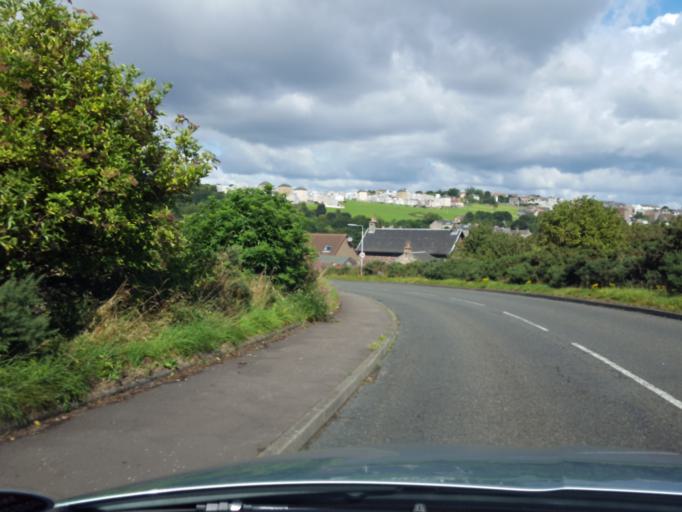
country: GB
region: Scotland
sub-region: Fife
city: Inverkeithing
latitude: 56.0210
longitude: -3.4013
